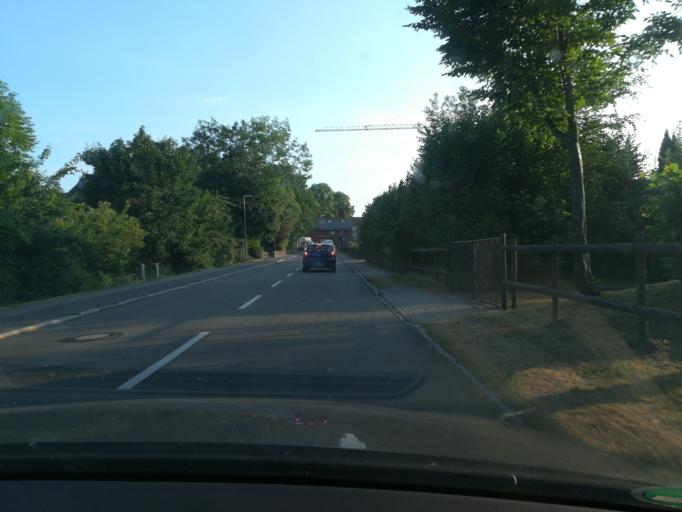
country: DE
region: Schleswig-Holstein
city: Grossensee
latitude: 53.6139
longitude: 10.3412
